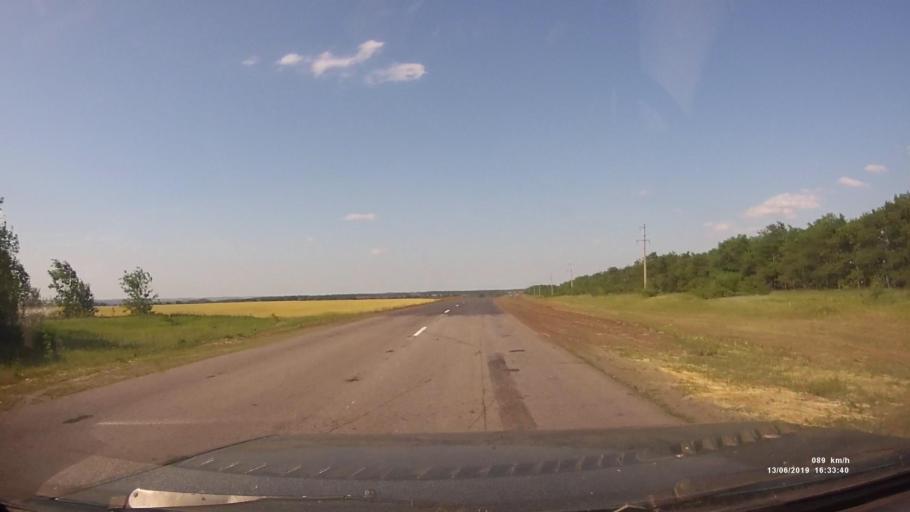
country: RU
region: Rostov
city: Kazanskaya
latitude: 49.8636
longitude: 41.2826
